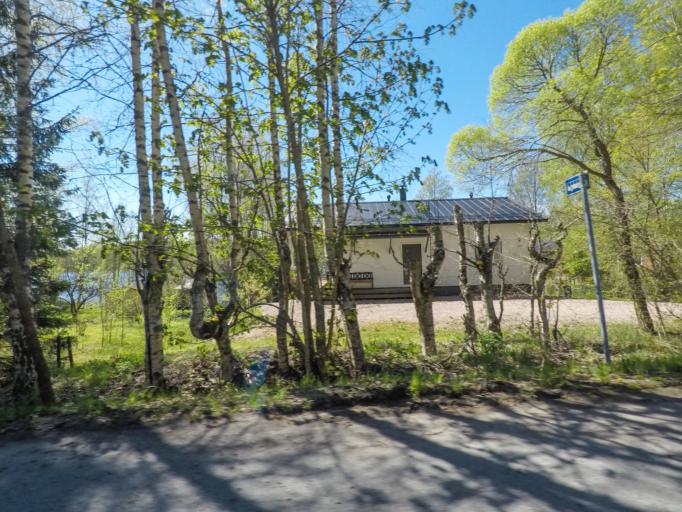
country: FI
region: Uusimaa
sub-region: Helsinki
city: Sammatti
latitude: 60.3443
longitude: 23.8012
